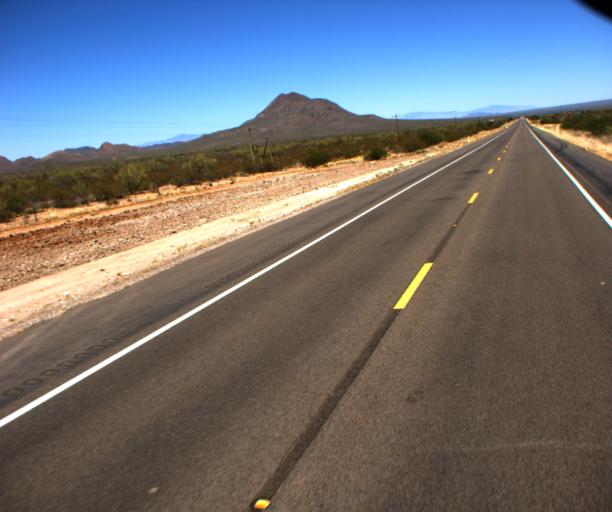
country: US
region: Arizona
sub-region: Pima County
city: Three Points
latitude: 32.0391
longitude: -111.4982
